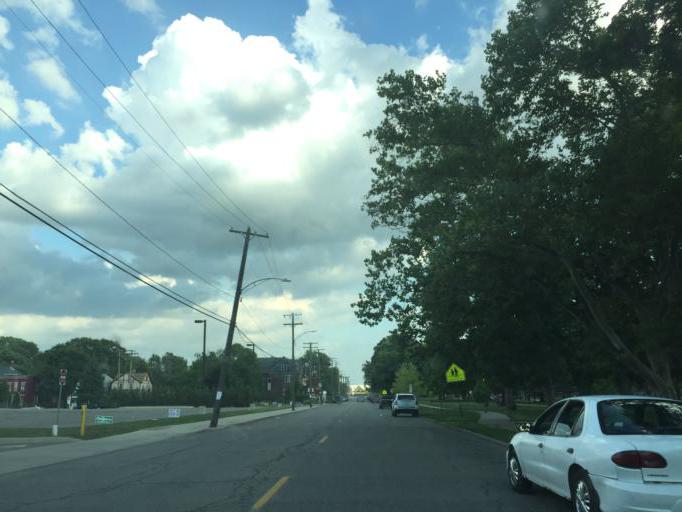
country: US
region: Michigan
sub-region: Wayne County
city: Detroit
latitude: 42.3184
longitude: -83.0921
